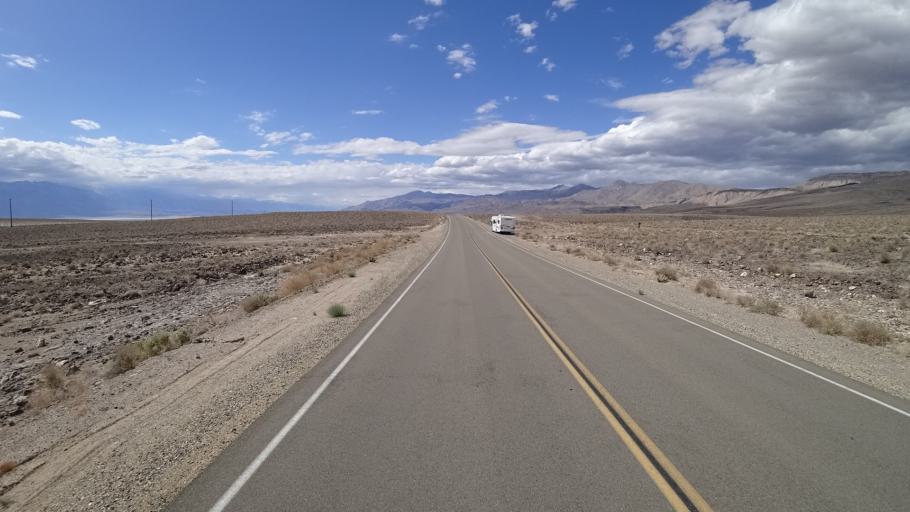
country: US
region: California
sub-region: Inyo County
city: Lone Pine
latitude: 36.4105
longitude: -117.8117
